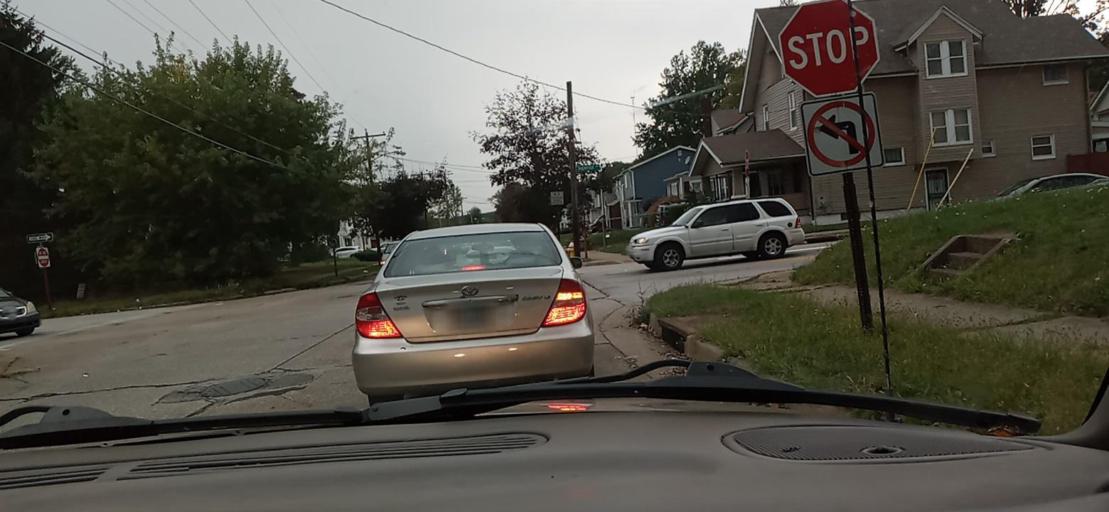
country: US
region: Ohio
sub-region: Summit County
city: Akron
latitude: 41.0616
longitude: -81.5582
